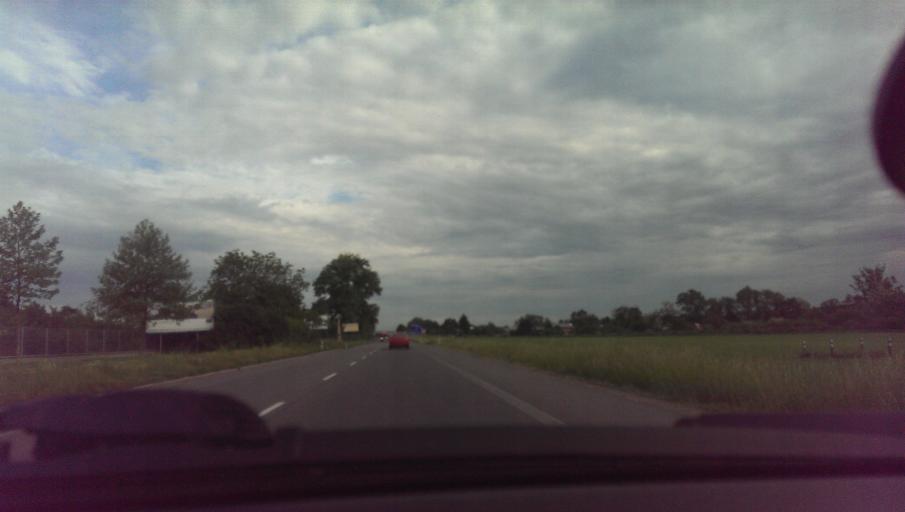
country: CZ
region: Zlin
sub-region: Okres Kromeriz
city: Kromeriz
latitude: 49.3069
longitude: 17.3800
